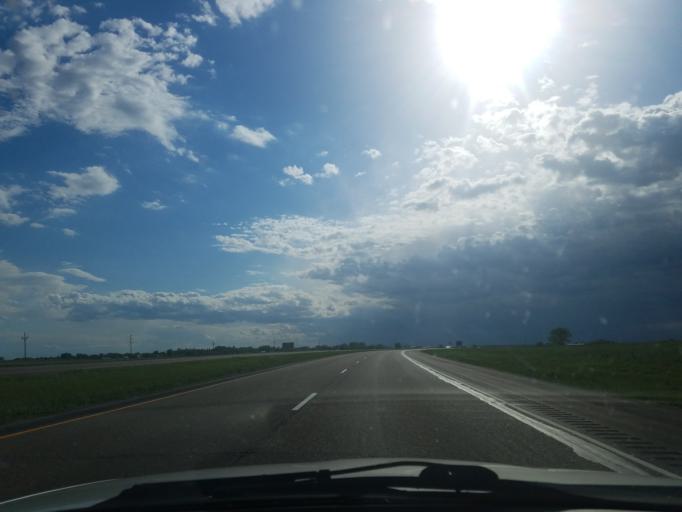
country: US
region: North Dakota
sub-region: Kidder County
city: Steele
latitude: 46.8651
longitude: -99.8946
